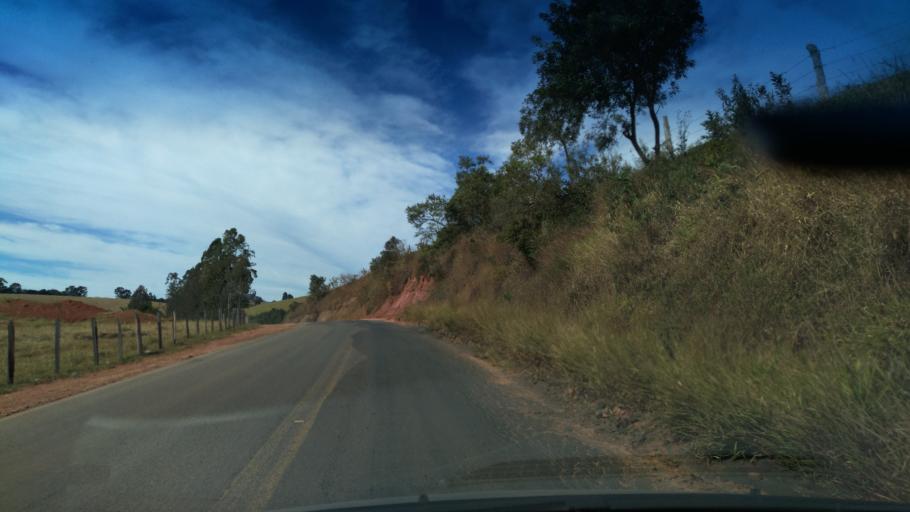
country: BR
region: Minas Gerais
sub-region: Andradas
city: Andradas
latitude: -22.0399
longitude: -46.3471
